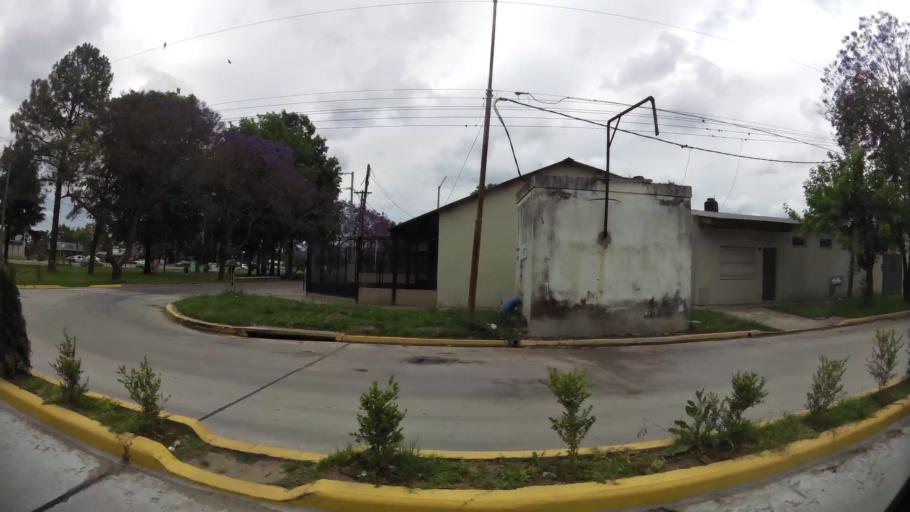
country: AR
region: Buenos Aires
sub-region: Partido de Zarate
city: Zarate
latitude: -34.1187
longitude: -59.0187
